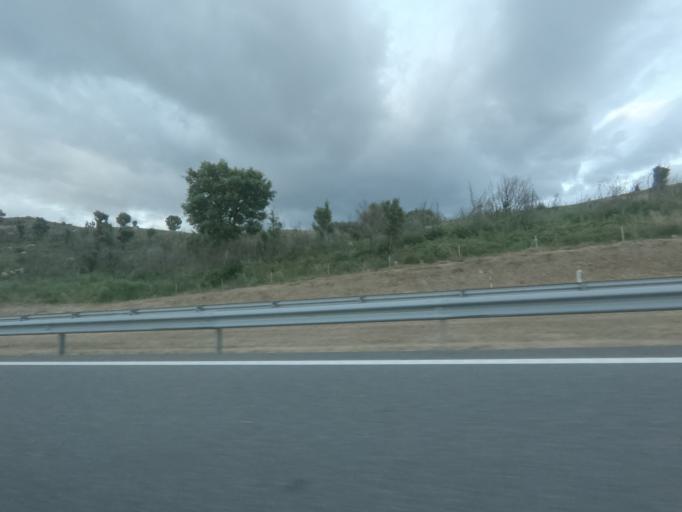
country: ES
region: Galicia
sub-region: Provincia de Ourense
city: Carballeda de Avia
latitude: 42.3018
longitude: -8.1798
